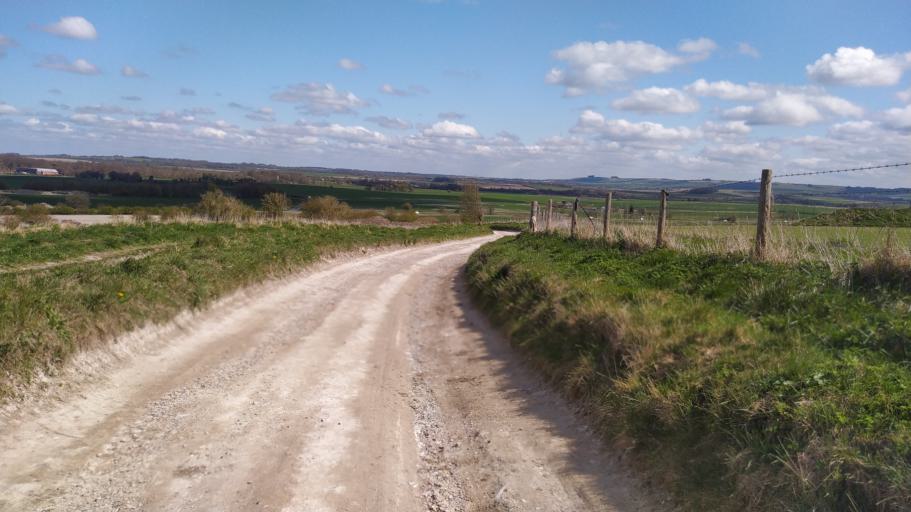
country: GB
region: England
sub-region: Wiltshire
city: Avebury
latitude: 51.4272
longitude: -1.9233
